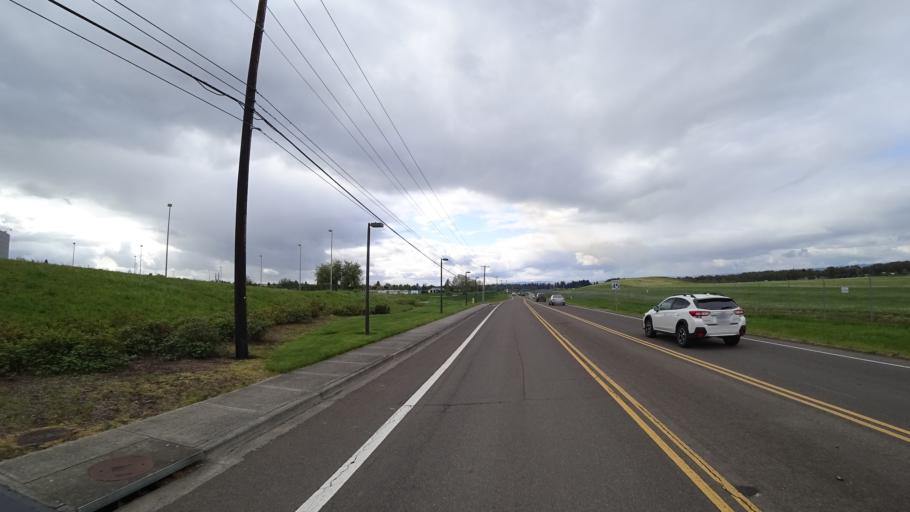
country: US
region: Oregon
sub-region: Washington County
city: Hillsboro
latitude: 45.5464
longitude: -122.9601
